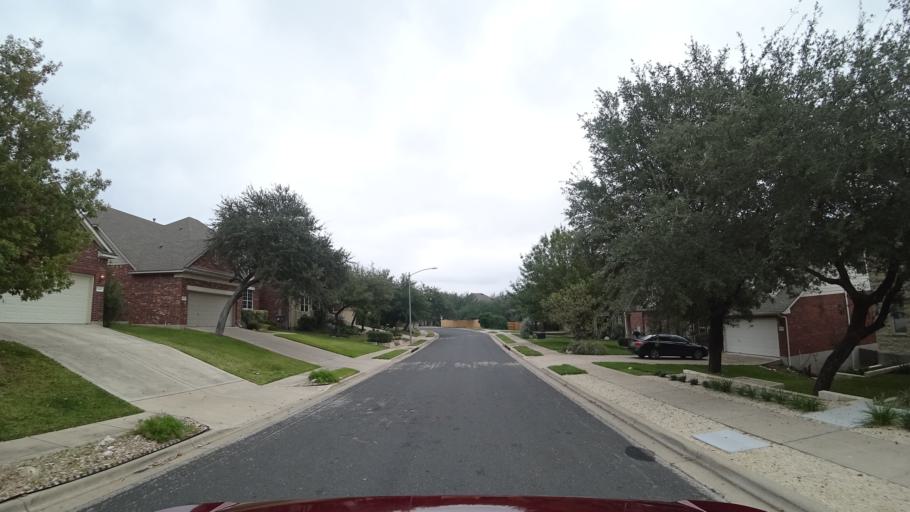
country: US
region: Texas
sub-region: Williamson County
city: Anderson Mill
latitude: 30.4298
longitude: -97.8191
